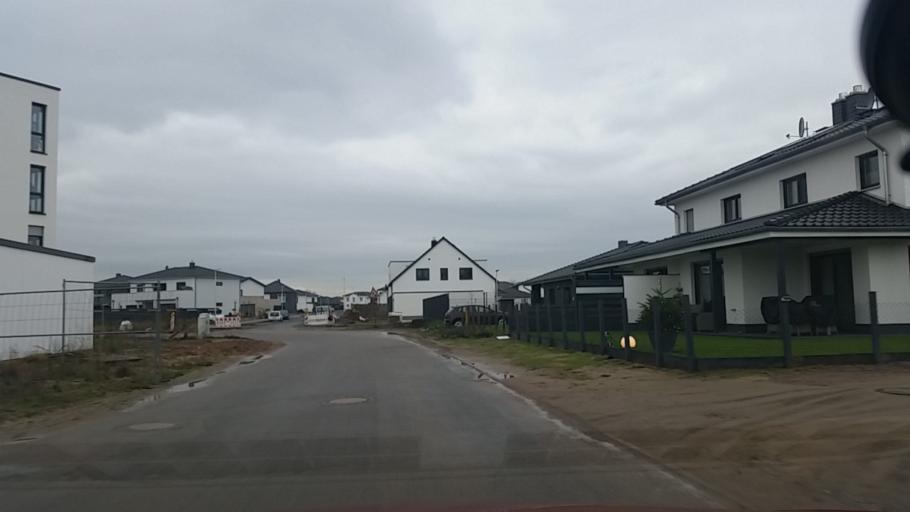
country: DE
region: Lower Saxony
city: Ruhen
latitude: 52.4618
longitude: 10.8425
